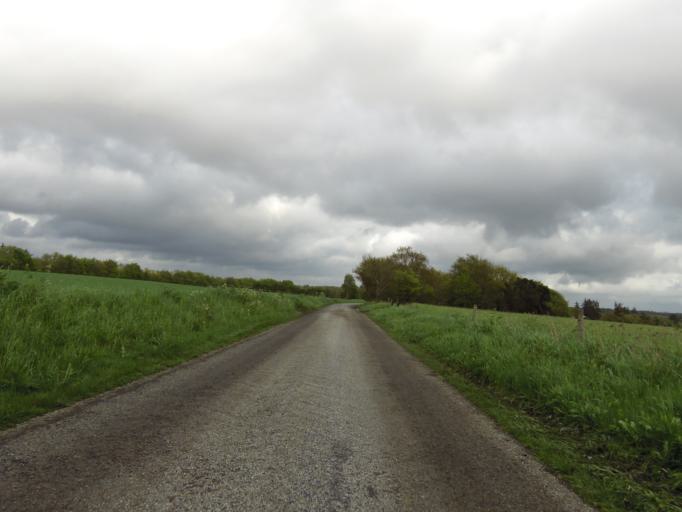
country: DK
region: South Denmark
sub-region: Haderslev Kommune
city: Gram
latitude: 55.2848
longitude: 8.9567
